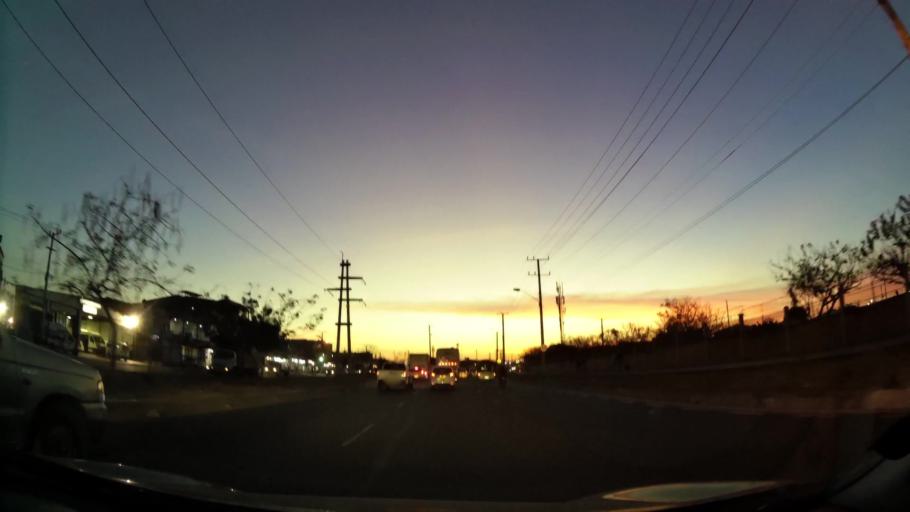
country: CO
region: Atlantico
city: Soledad
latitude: 10.9251
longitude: -74.7913
